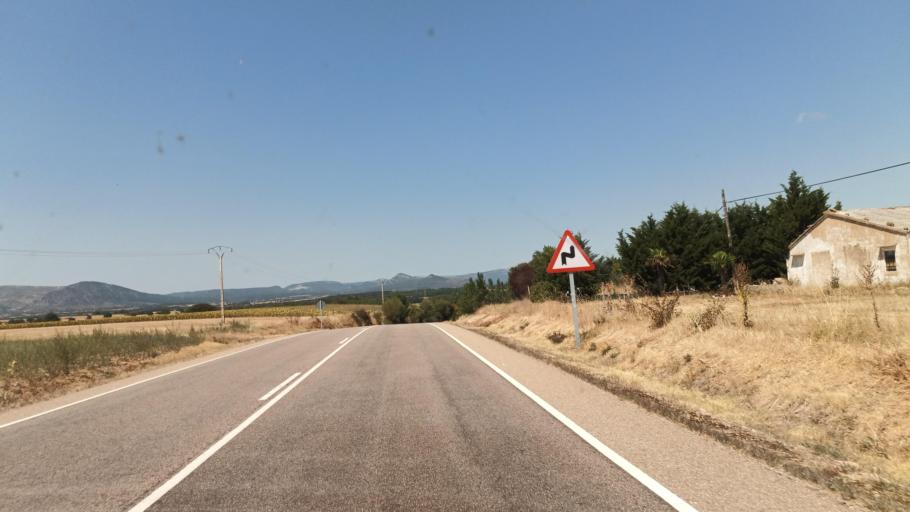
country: ES
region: Castille and Leon
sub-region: Provincia de Burgos
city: Quintanabureba
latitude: 42.6373
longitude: -3.3847
